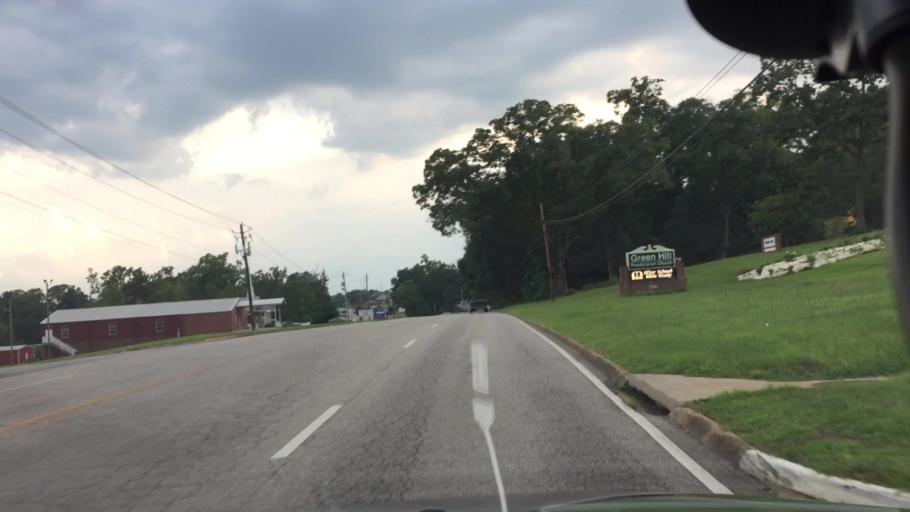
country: US
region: Alabama
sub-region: Coffee County
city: Enterprise
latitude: 31.3246
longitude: -85.8443
